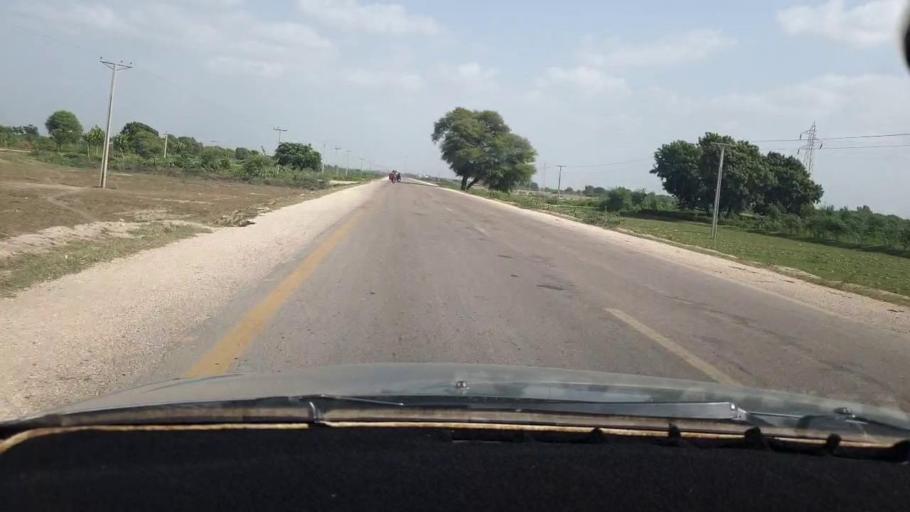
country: PK
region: Sindh
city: Naukot
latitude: 24.8750
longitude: 69.3682
